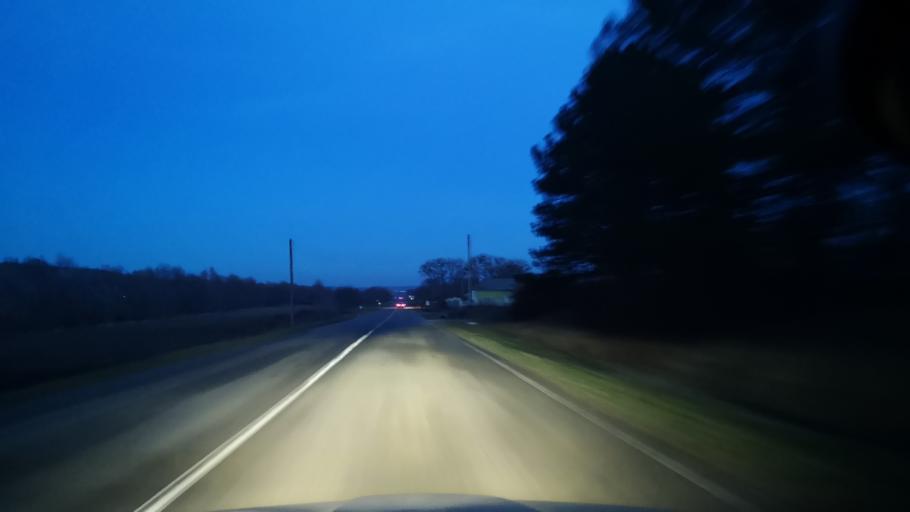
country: MD
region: Orhei
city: Orhei
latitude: 47.3430
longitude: 28.6796
